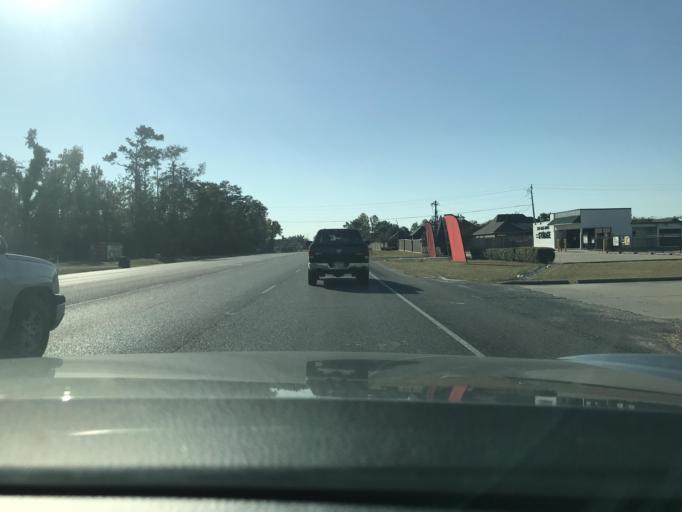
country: US
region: Louisiana
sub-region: Calcasieu Parish
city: Moss Bluff
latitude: 30.3008
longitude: -93.2360
